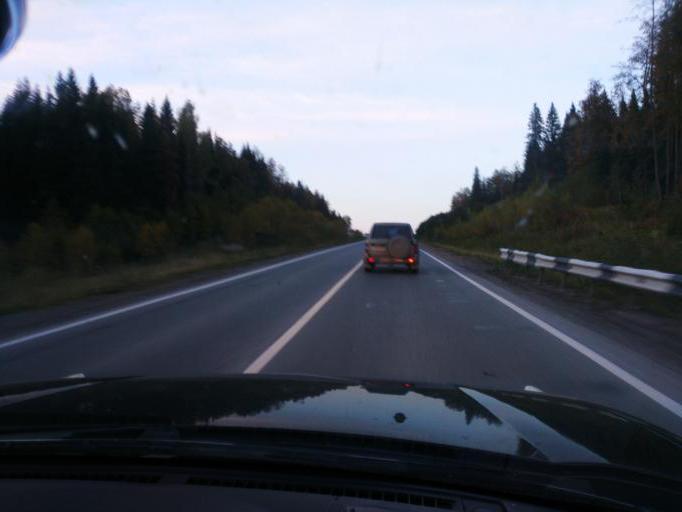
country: RU
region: Perm
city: Sylva
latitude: 58.2851
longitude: 56.7381
